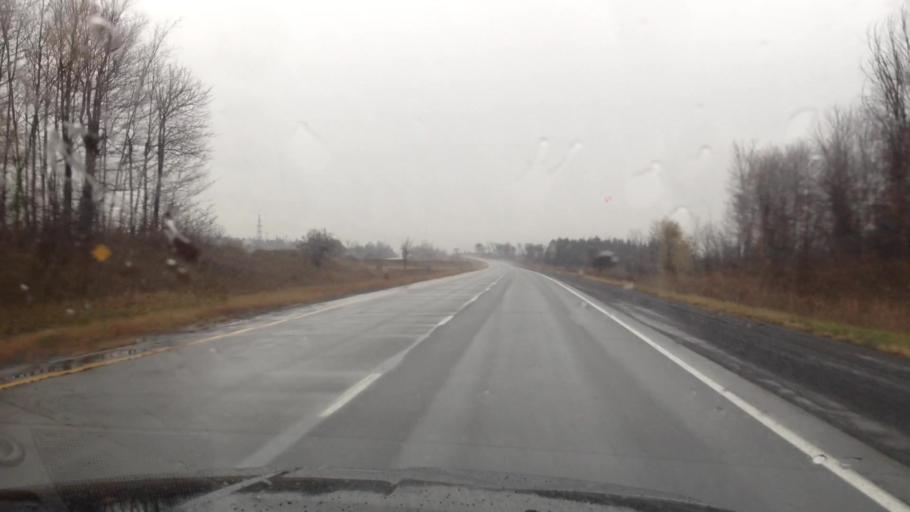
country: CA
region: Ontario
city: Casselman
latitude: 45.3674
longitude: -74.8622
